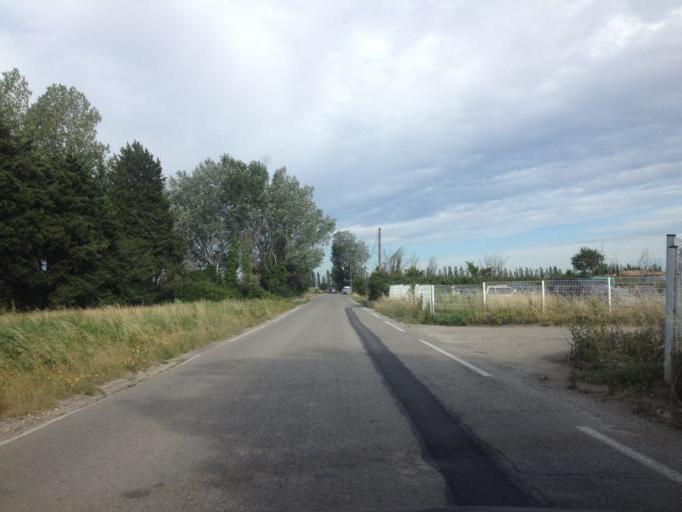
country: FR
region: Provence-Alpes-Cote d'Azur
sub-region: Departement du Vaucluse
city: Orange
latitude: 44.1218
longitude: 4.7966
